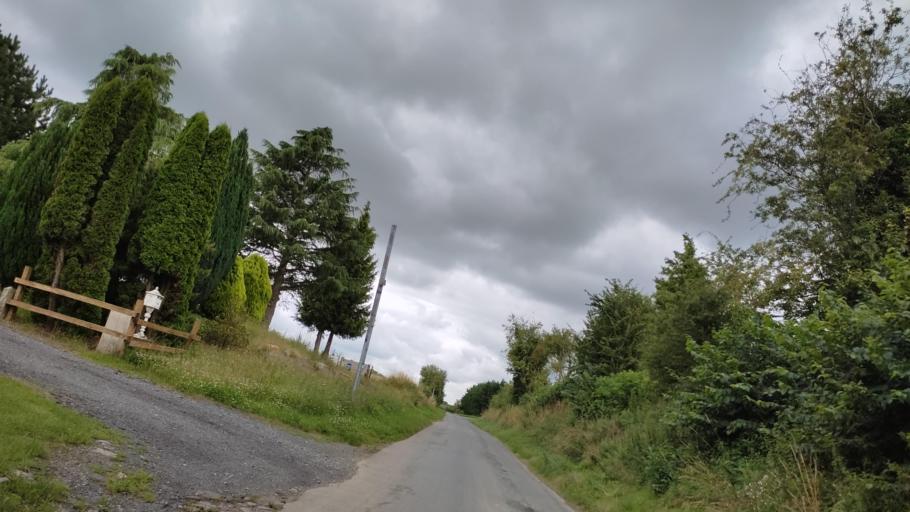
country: FR
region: Nord-Pas-de-Calais
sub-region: Departement du Pas-de-Calais
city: Dainville
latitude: 50.2757
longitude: 2.7122
